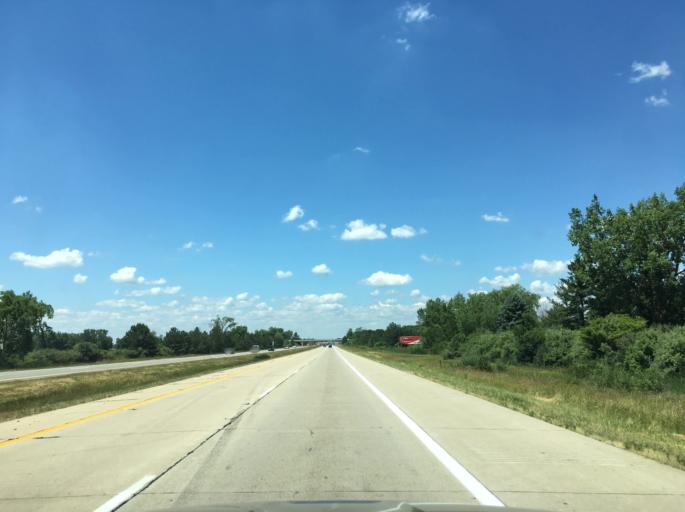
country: US
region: Michigan
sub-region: Bay County
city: Auburn
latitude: 43.5975
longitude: -84.1210
